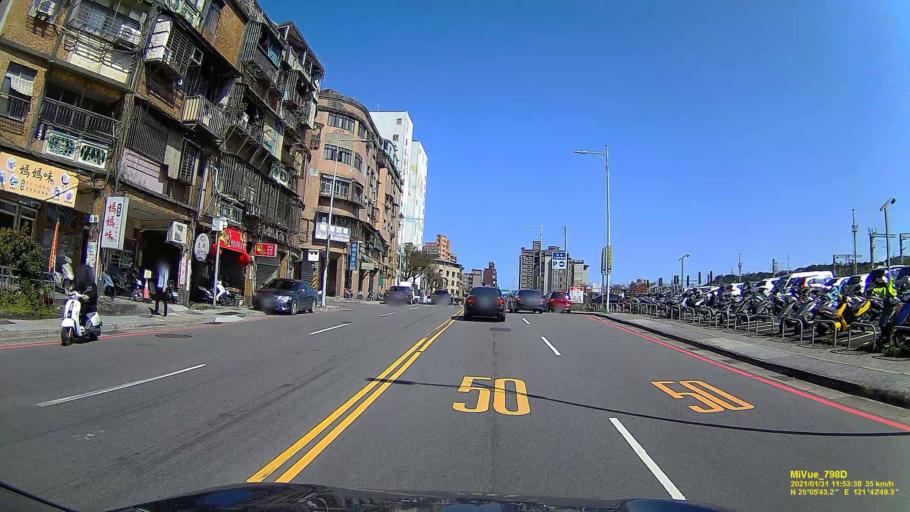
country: TW
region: Taiwan
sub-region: Keelung
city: Keelung
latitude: 25.0955
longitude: 121.7138
